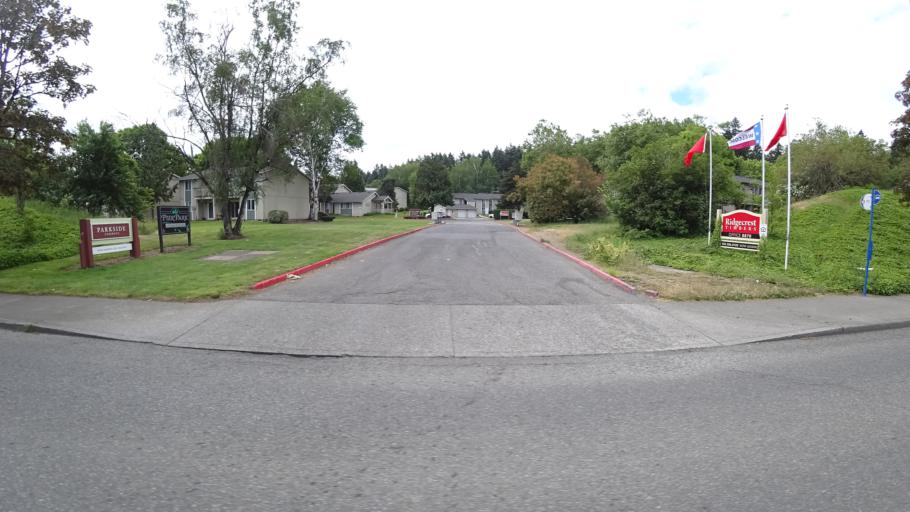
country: US
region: Oregon
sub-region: Washington County
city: West Haven
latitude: 45.6038
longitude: -122.7500
